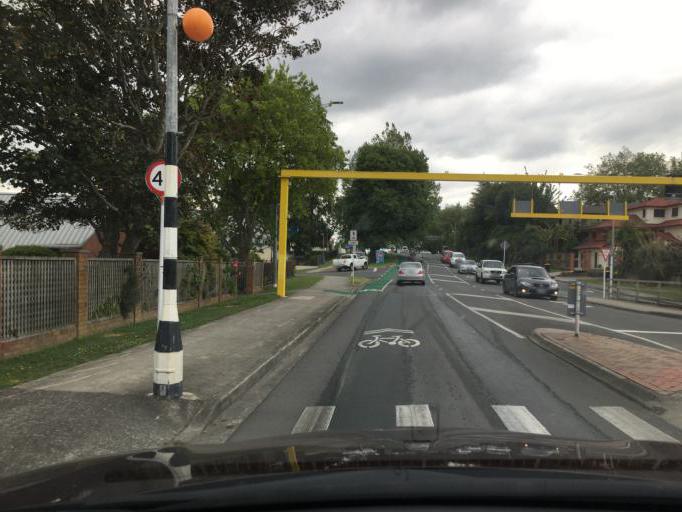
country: NZ
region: Waikato
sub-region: Waipa District
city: Cambridge
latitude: -37.8982
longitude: 175.4736
